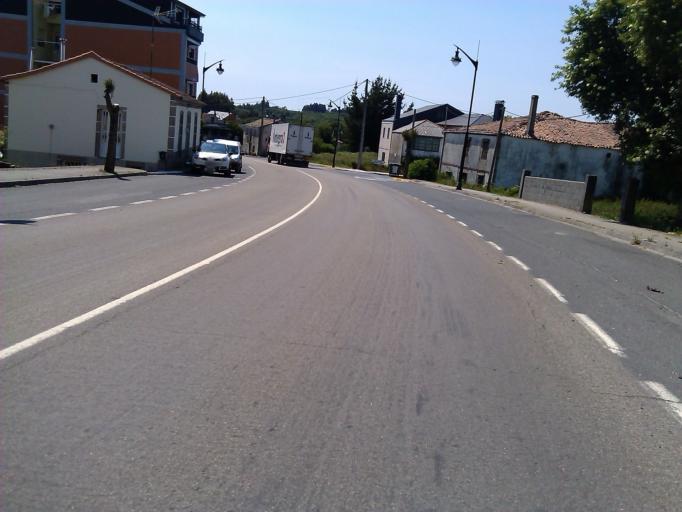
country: ES
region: Galicia
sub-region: Provincia de Lugo
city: Monterroso
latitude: 42.8740
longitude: -7.8714
